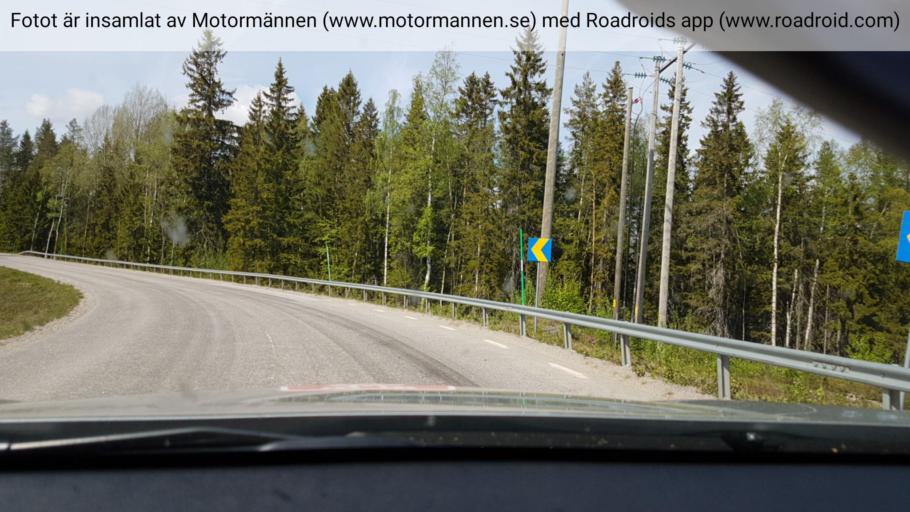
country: SE
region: Vaesterbotten
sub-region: Umea Kommun
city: Roback
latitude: 63.8590
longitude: 20.0761
